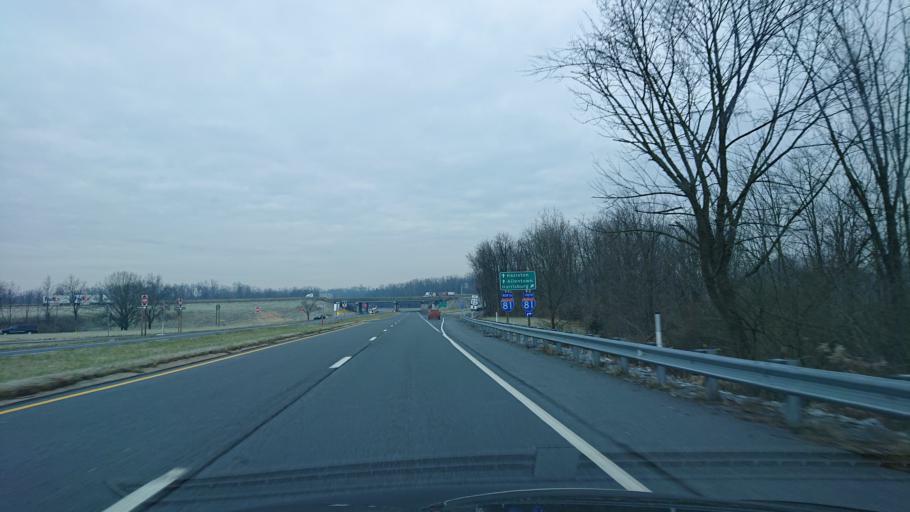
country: US
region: Pennsylvania
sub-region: Lebanon County
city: Jonestown
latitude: 40.4167
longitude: -76.5800
